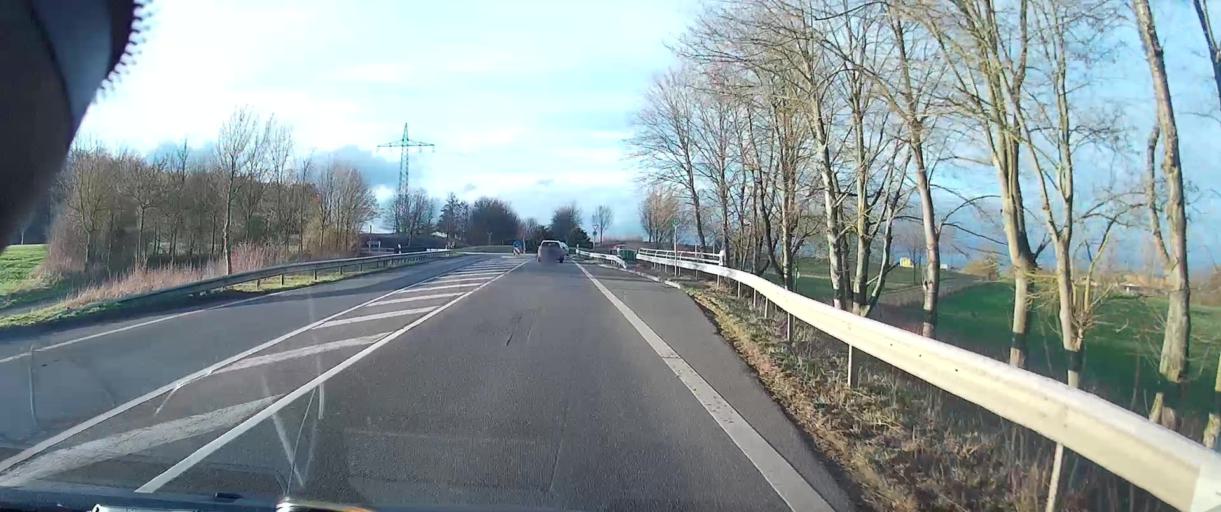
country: DE
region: Rheinland-Pfalz
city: Dernbach
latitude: 50.4571
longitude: 7.8060
